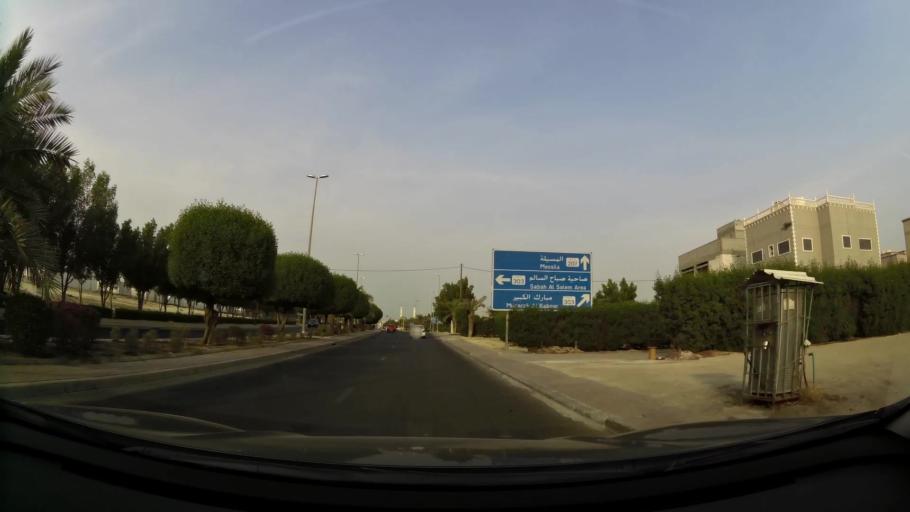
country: KW
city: Al Funaytis
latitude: 29.2241
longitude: 48.0802
